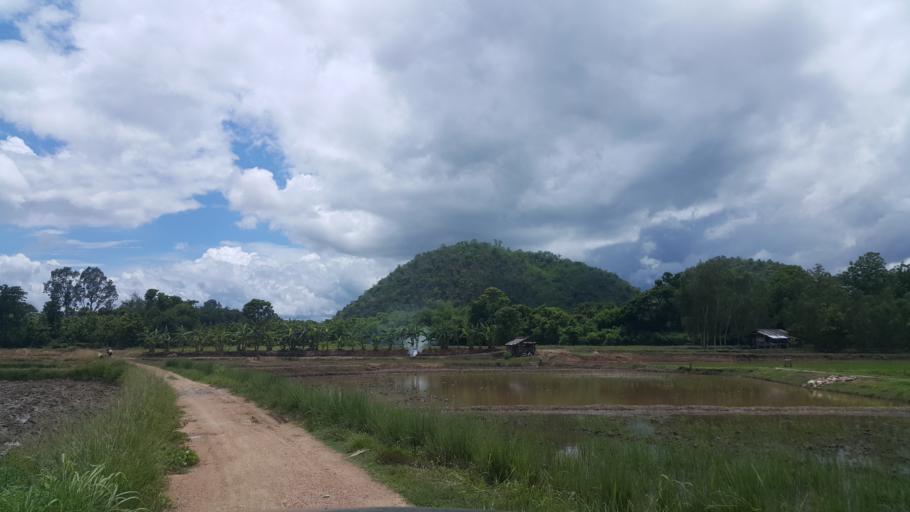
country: TH
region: Sukhothai
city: Thung Saliam
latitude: 17.3341
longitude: 99.4653
